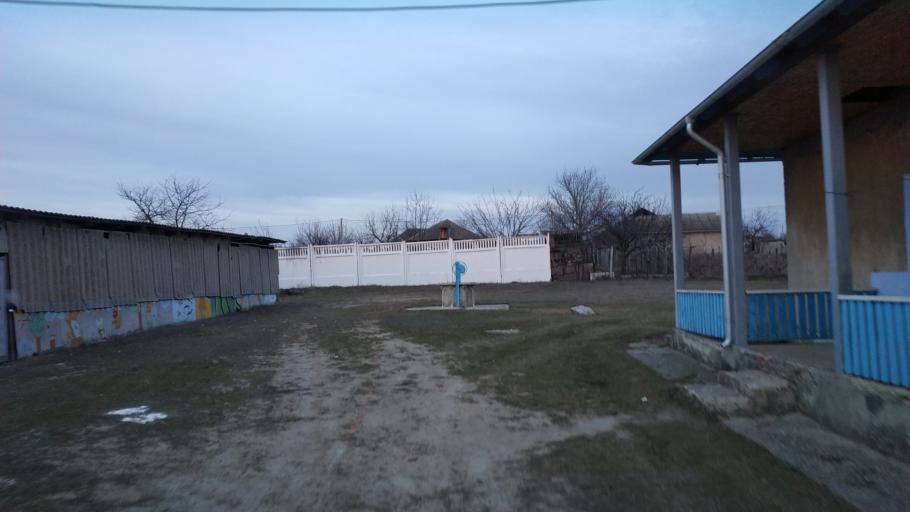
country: MD
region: Hincesti
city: Dancu
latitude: 46.7400
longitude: 28.2225
